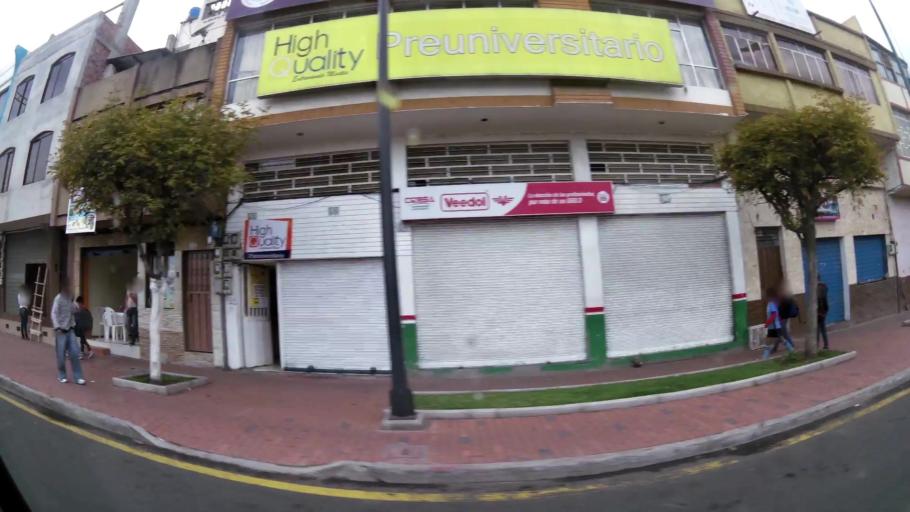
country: EC
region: Tungurahua
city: Ambato
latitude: -1.2353
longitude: -78.6225
